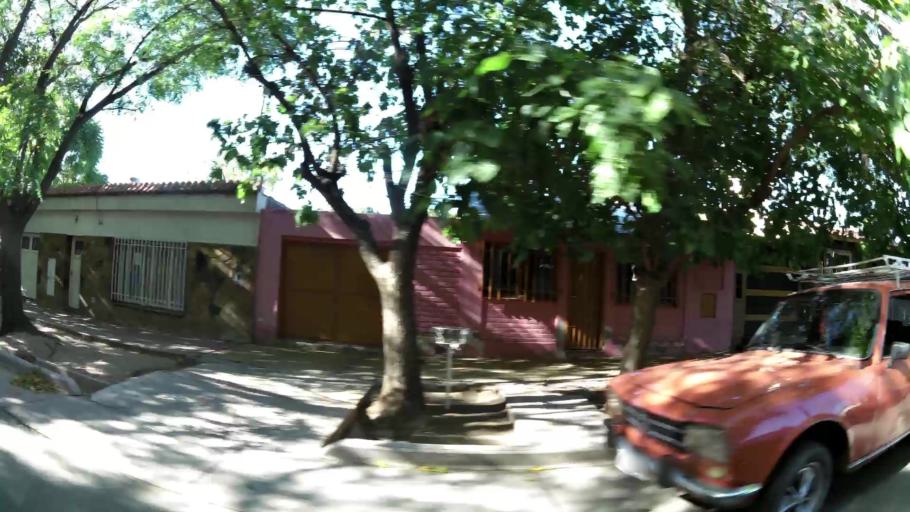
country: AR
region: Mendoza
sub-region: Departamento de Godoy Cruz
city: Godoy Cruz
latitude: -32.9221
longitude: -68.8558
